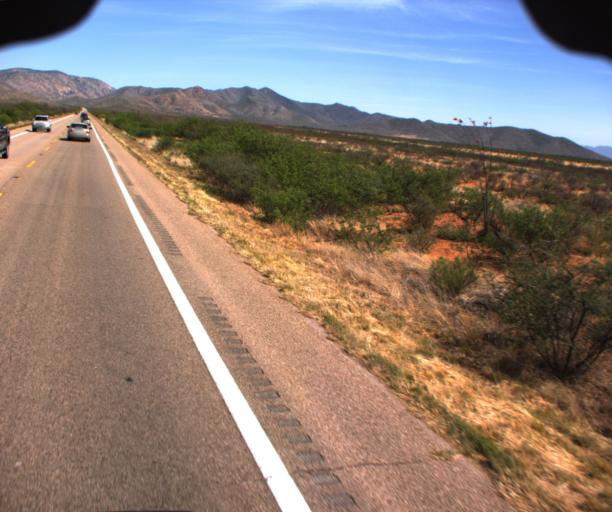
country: US
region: Arizona
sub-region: Cochise County
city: Bisbee
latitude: 31.5369
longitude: -110.0670
